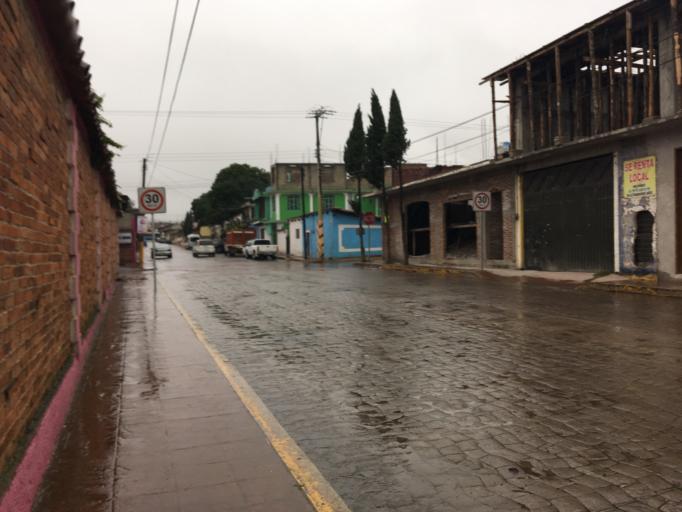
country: MX
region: Puebla
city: Chignahuapan
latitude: 19.8396
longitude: -98.0278
